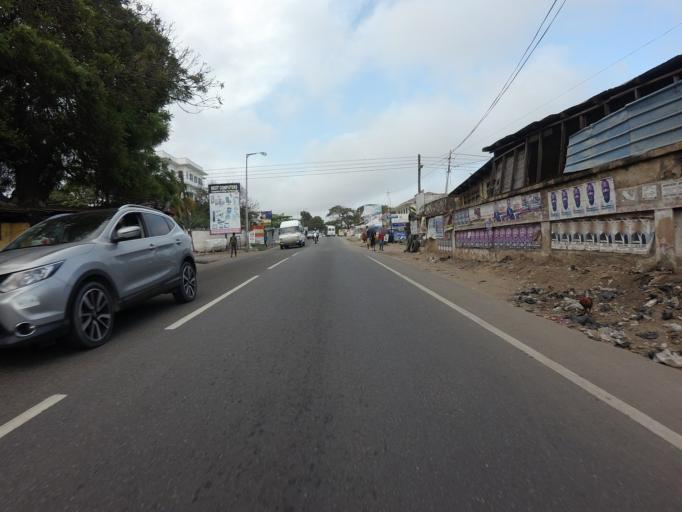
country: GH
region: Greater Accra
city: Accra
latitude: 5.5512
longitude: -0.1808
